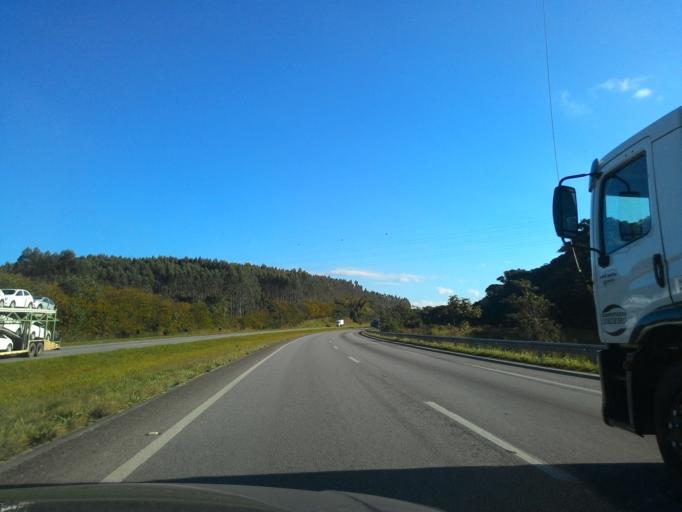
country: BR
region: Sao Paulo
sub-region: Registro
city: Registro
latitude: -24.5641
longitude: -47.8698
